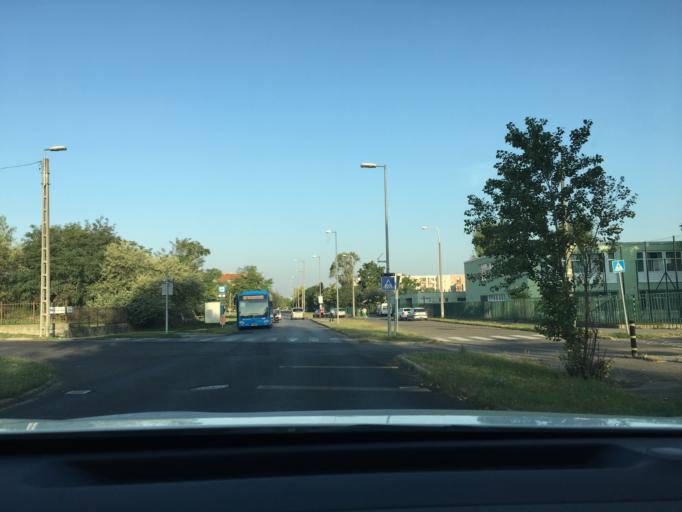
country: HU
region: Budapest
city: Budapest XVII. keruelet
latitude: 47.4787
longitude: 19.2379
